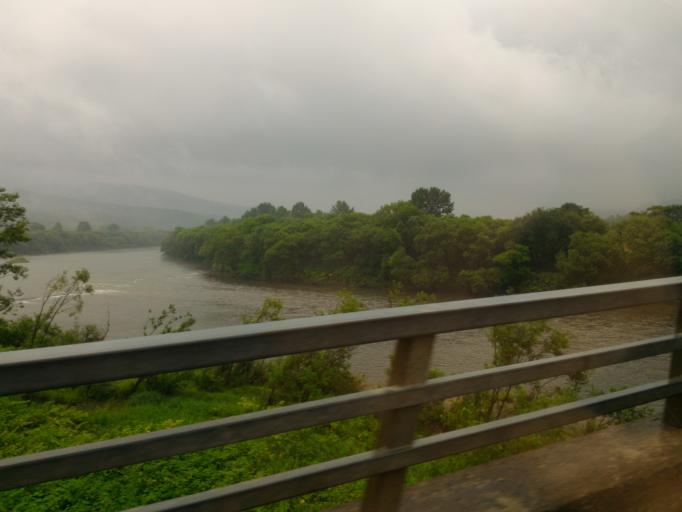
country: JP
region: Hokkaido
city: Nayoro
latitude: 44.5923
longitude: 142.3079
